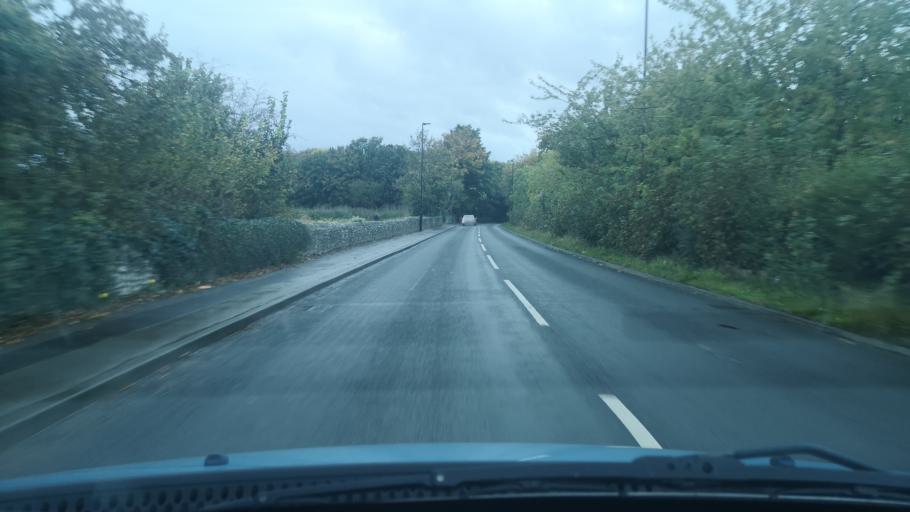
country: GB
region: England
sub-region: Doncaster
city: Askern
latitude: 53.6185
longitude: -1.1639
